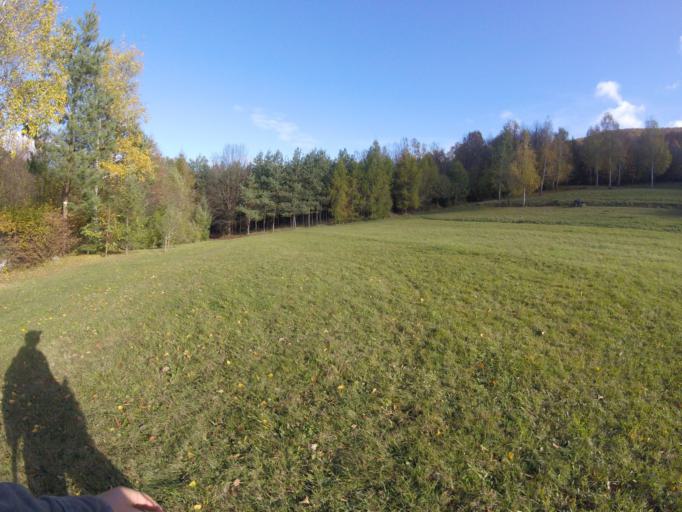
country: HU
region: Borsod-Abauj-Zemplen
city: Tolcsva
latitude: 48.3783
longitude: 21.3812
